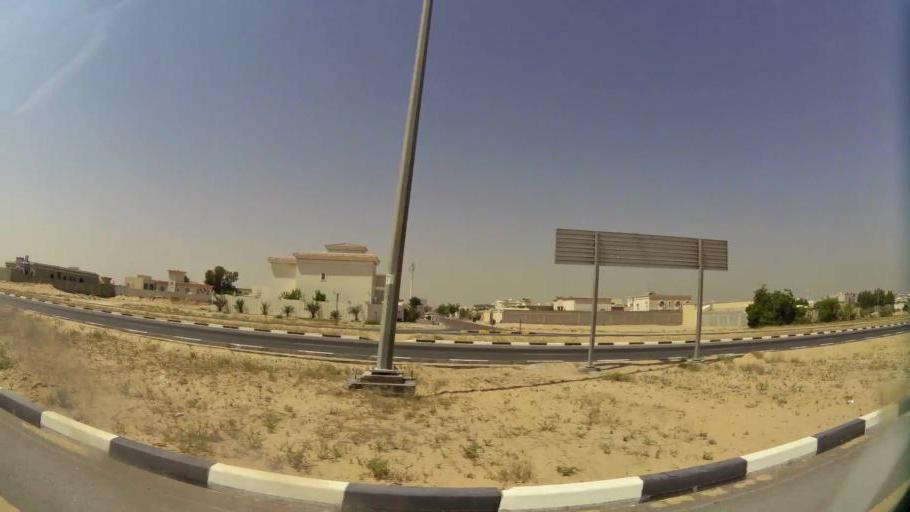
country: AE
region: Ajman
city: Ajman
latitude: 25.4247
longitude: 55.5263
